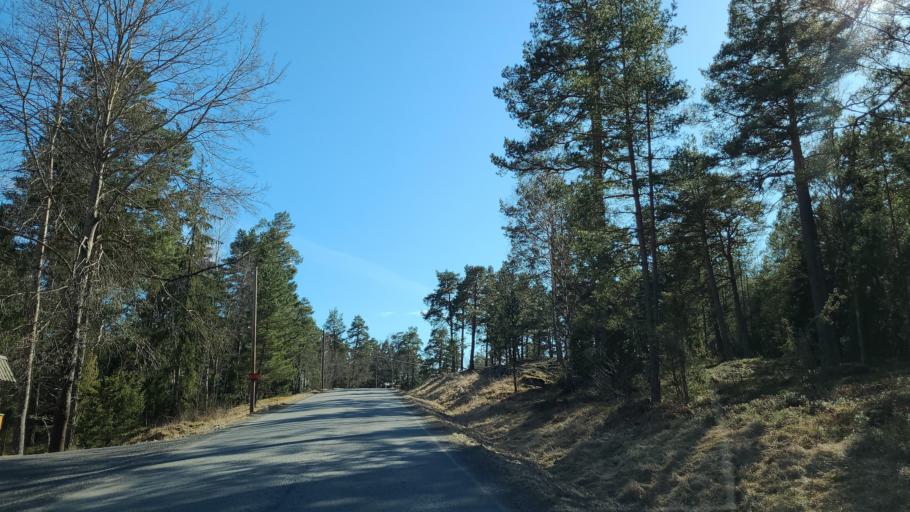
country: SE
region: Stockholm
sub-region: Varmdo Kommun
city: Hemmesta
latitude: 59.2794
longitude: 18.5698
